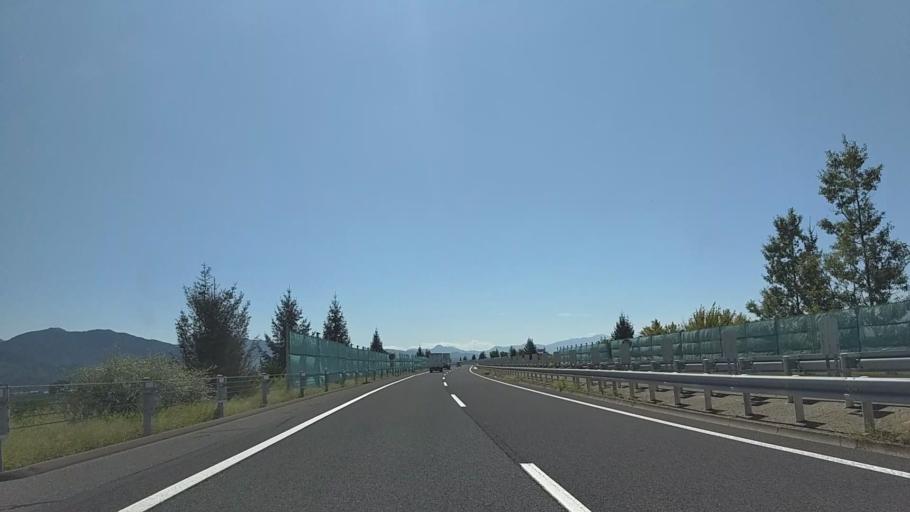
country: JP
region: Nagano
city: Suzaka
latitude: 36.6742
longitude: 138.2882
